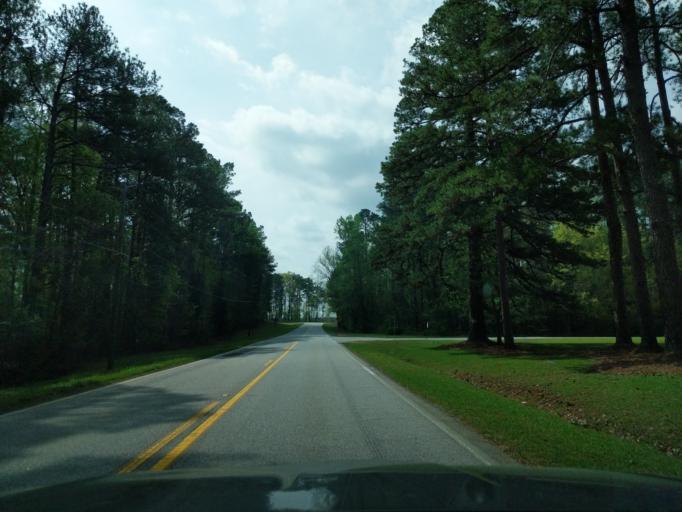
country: US
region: Georgia
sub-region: Columbia County
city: Appling
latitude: 33.5873
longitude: -82.3177
